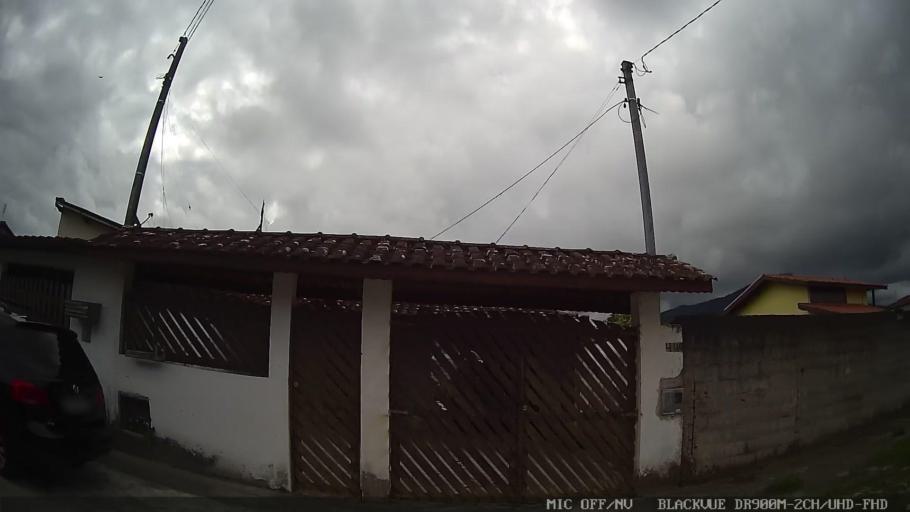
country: BR
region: Sao Paulo
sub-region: Caraguatatuba
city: Caraguatatuba
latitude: -23.6428
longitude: -45.4406
